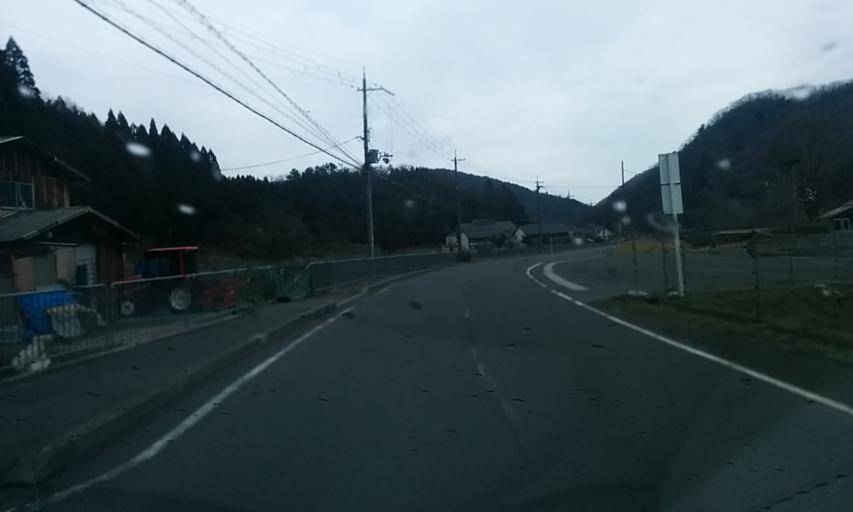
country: JP
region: Hyogo
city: Sasayama
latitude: 35.1327
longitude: 135.4128
